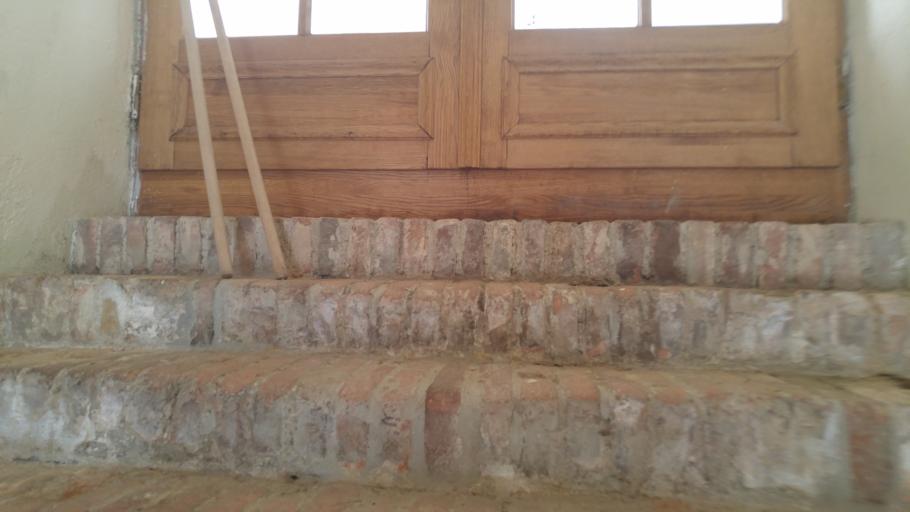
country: CZ
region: Praha
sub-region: Praha 1
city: Mala Strana
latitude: 50.0862
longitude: 14.3564
